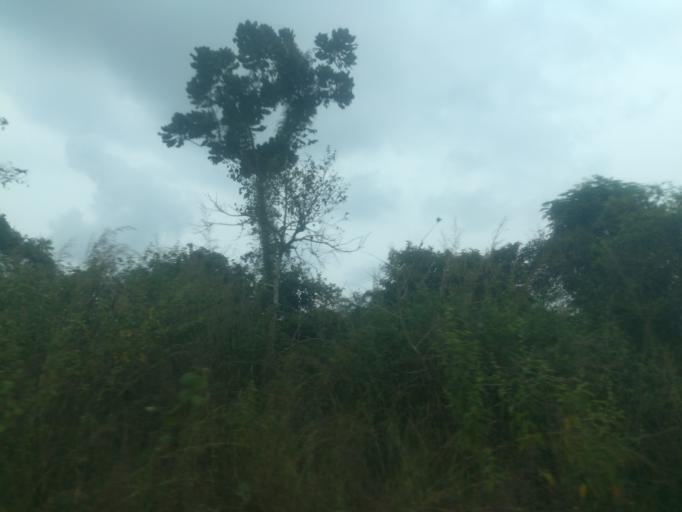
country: NG
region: Ogun
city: Itori
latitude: 7.1017
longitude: 3.1531
